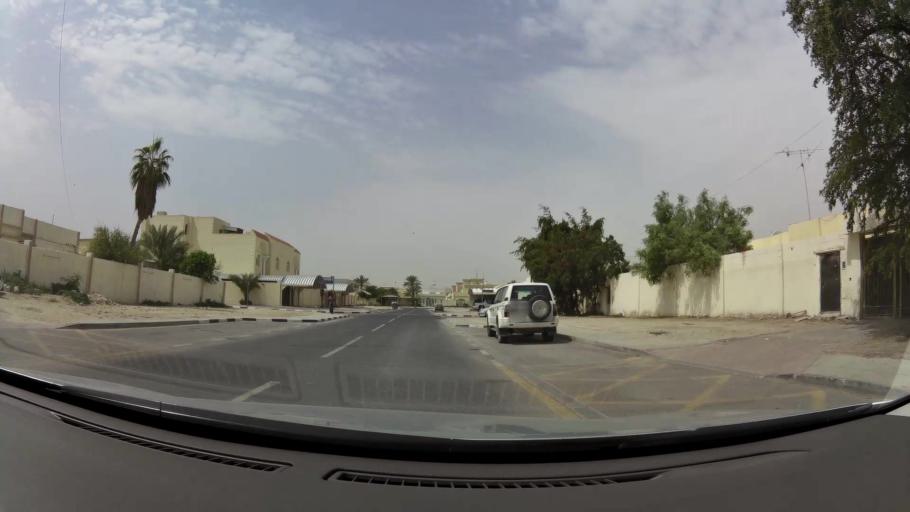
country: QA
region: Baladiyat ad Dawhah
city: Doha
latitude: 25.3090
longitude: 51.4816
